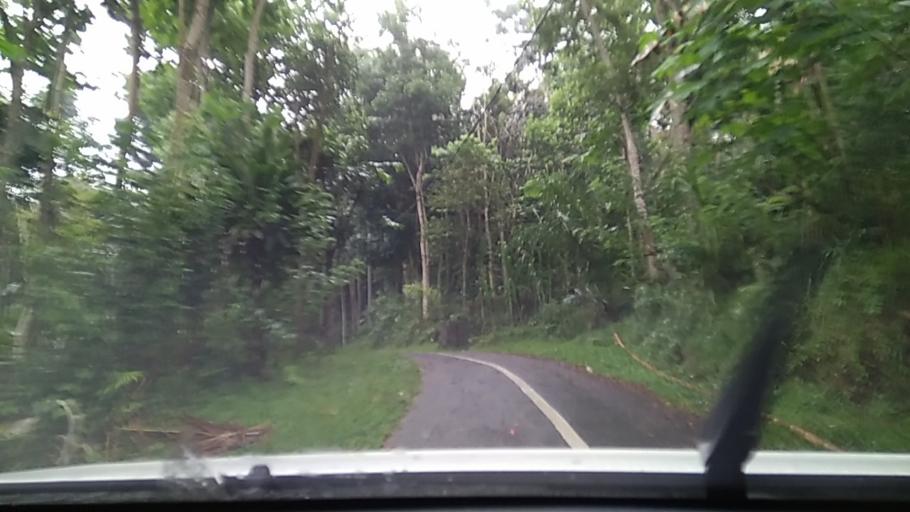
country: ID
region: Bali
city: Tiyingtali Kelod
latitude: -8.3999
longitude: 115.6305
